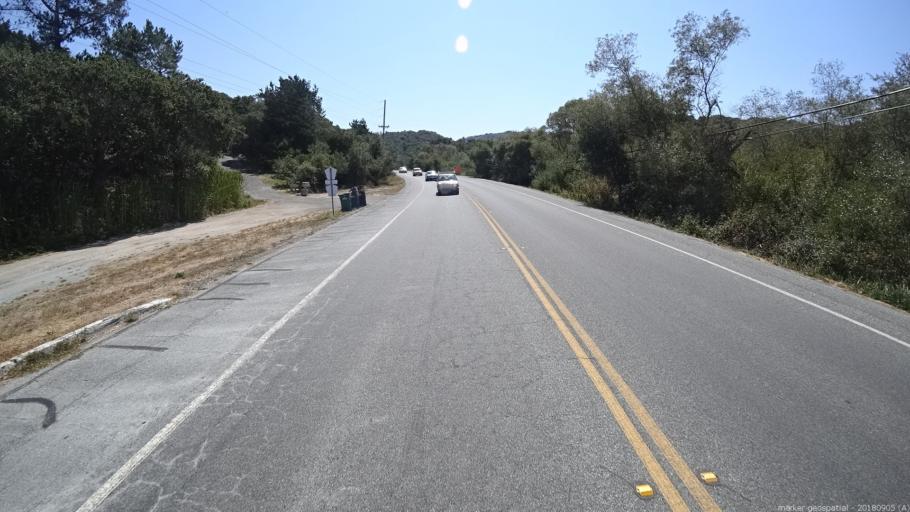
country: US
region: California
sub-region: Monterey County
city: Carmel Valley Village
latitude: 36.5678
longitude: -121.7554
